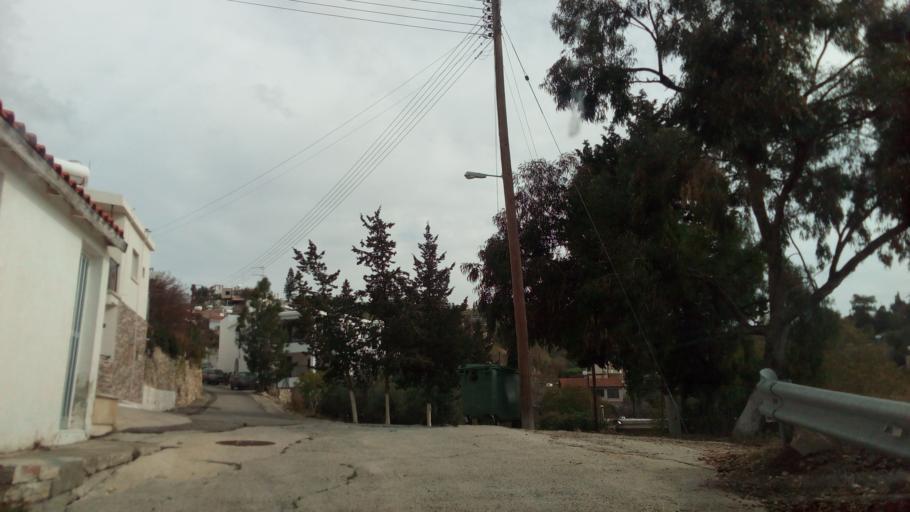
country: CY
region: Pafos
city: Mesogi
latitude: 34.7984
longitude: 32.4776
